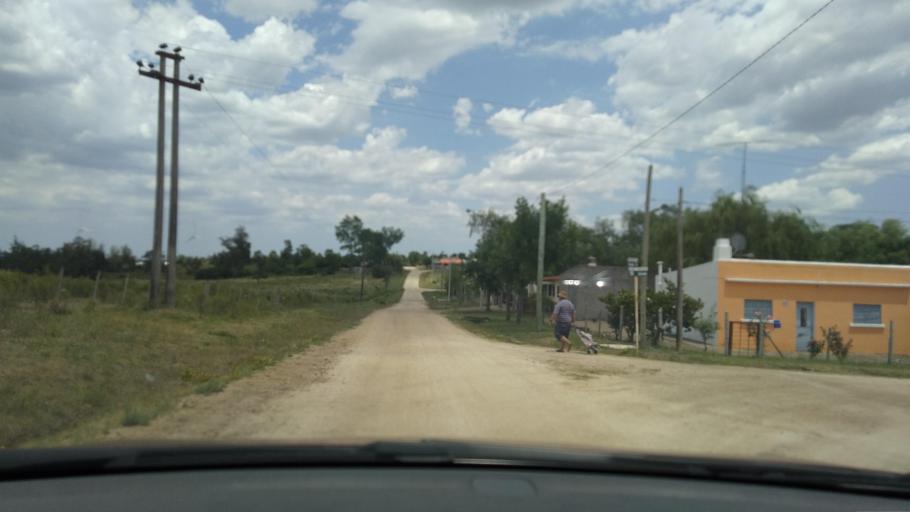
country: UY
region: Canelones
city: Tala
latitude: -34.1962
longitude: -55.7316
